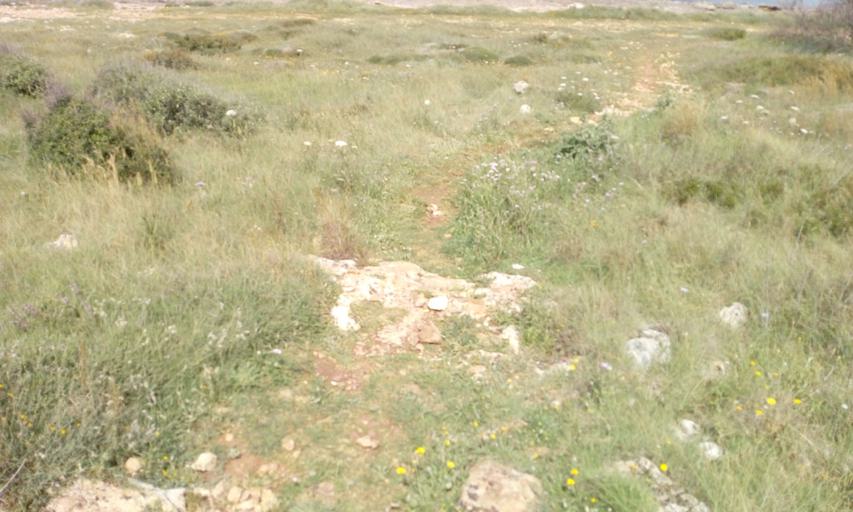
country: IT
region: Apulia
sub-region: Provincia di Lecce
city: Gallipoli
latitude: 39.9971
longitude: 17.9999
